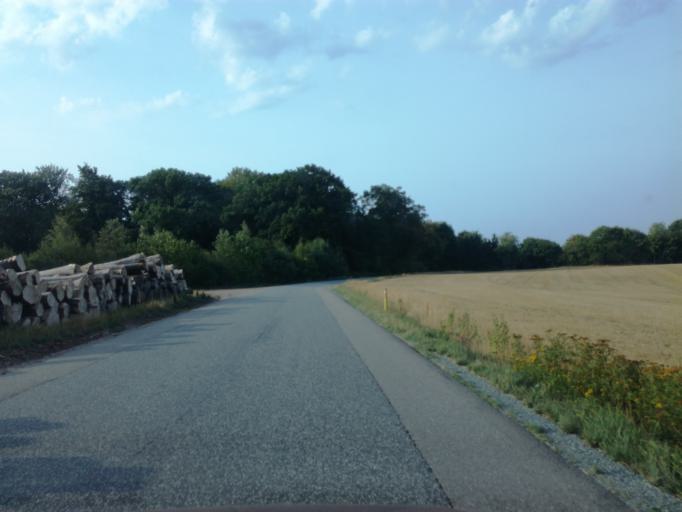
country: DK
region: South Denmark
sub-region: Vejle Kommune
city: Vejle
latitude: 55.6609
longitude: 9.5474
